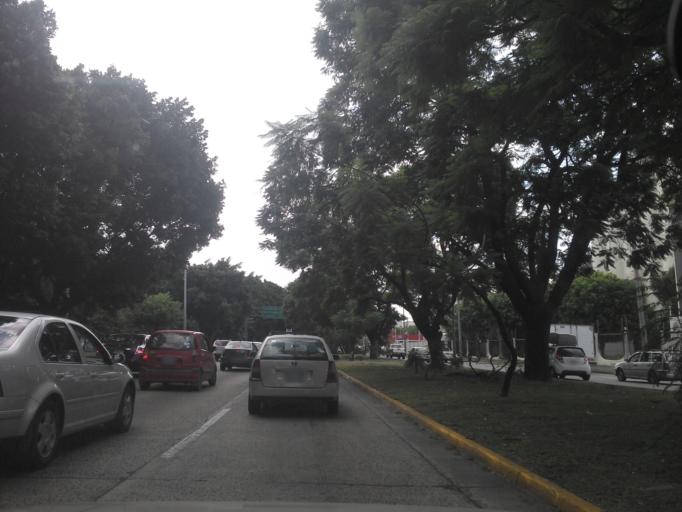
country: MX
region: Jalisco
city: Guadalajara
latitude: 20.6447
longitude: -103.3569
